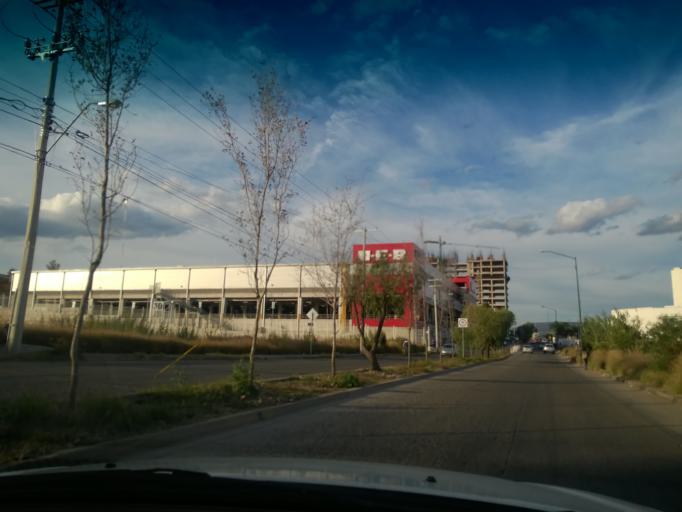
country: MX
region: Guanajuato
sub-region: Leon
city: La Ermita
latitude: 21.1555
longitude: -101.7022
